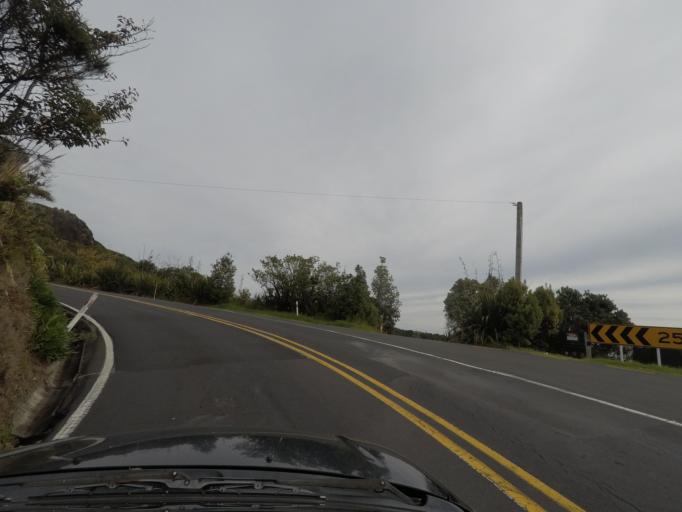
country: NZ
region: Auckland
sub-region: Auckland
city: Muriwai Beach
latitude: -36.9610
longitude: 174.4751
